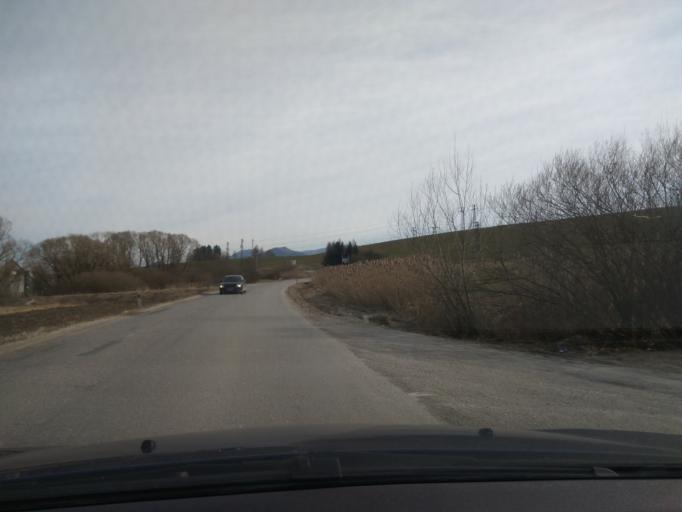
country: SK
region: Zilinsky
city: Rajec
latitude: 49.0848
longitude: 18.6197
